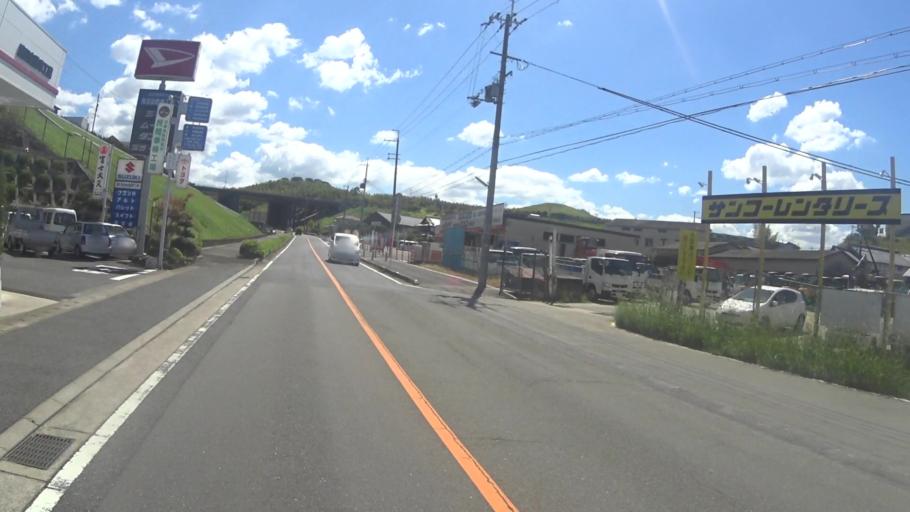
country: JP
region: Nara
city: Nara-shi
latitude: 34.7181
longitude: 135.8261
